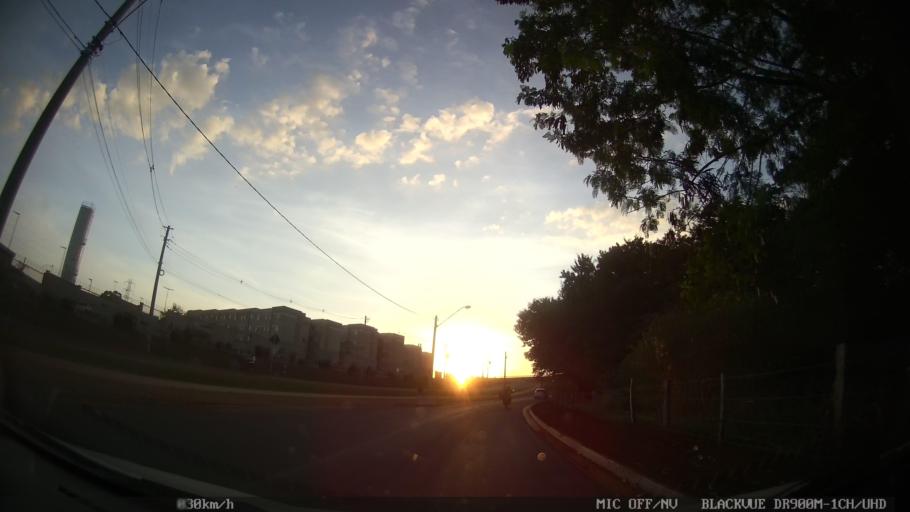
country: BR
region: Sao Paulo
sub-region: Ribeirao Preto
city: Ribeirao Preto
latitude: -21.1190
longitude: -47.8262
